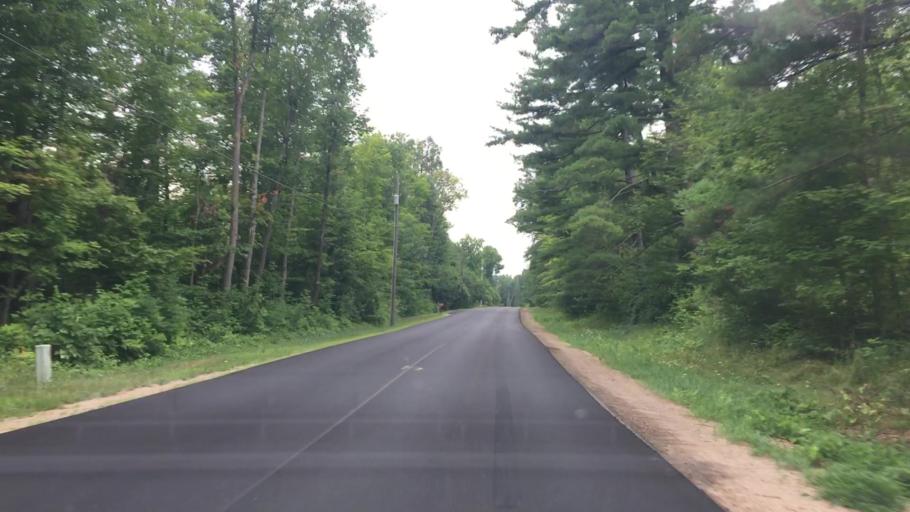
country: US
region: New York
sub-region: Clinton County
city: Peru
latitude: 44.5564
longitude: -73.5662
